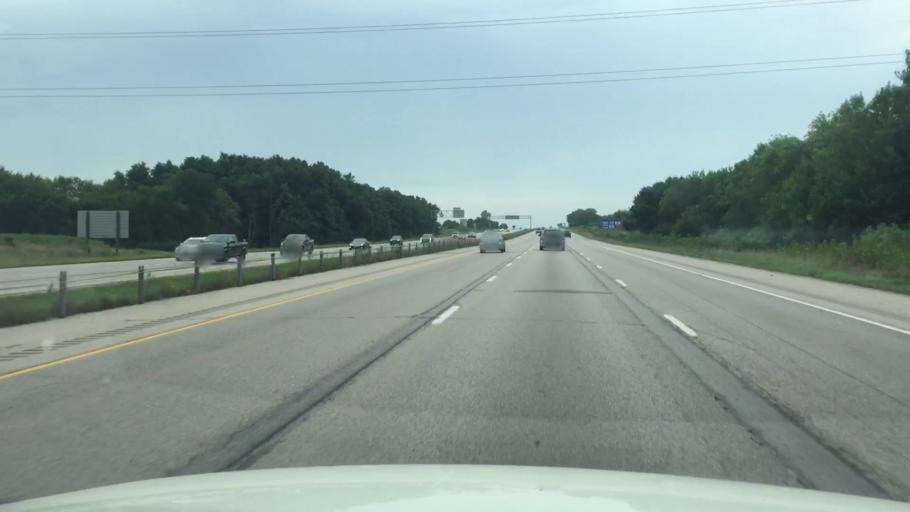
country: US
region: Iowa
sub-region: Polk County
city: Ankeny
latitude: 41.7177
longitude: -93.5767
